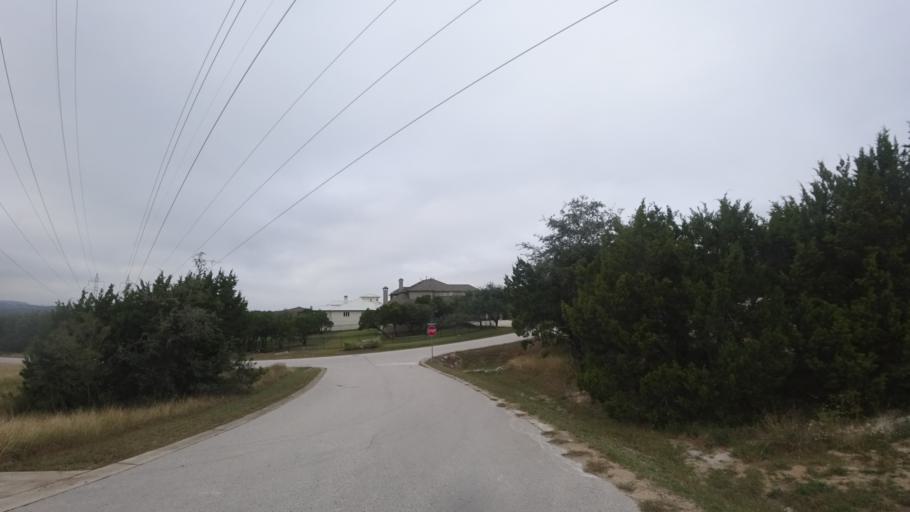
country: US
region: Texas
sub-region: Travis County
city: Hudson Bend
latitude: 30.3896
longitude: -97.9191
